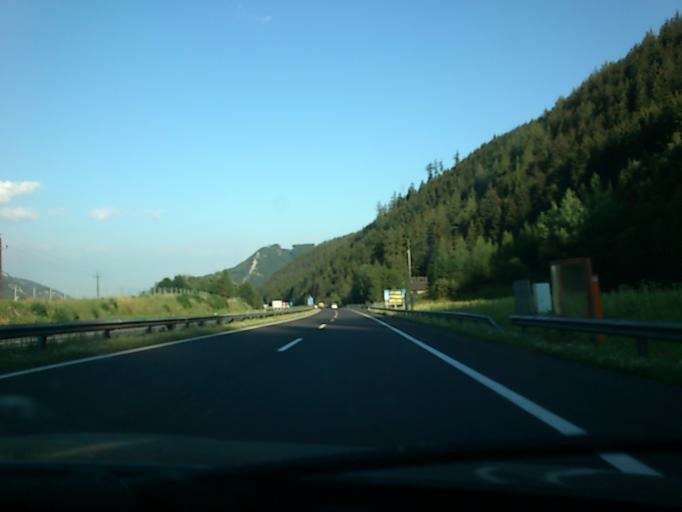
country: AT
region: Styria
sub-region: Politischer Bezirk Leoben
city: Mautern in Steiermark
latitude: 47.3994
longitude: 14.7919
